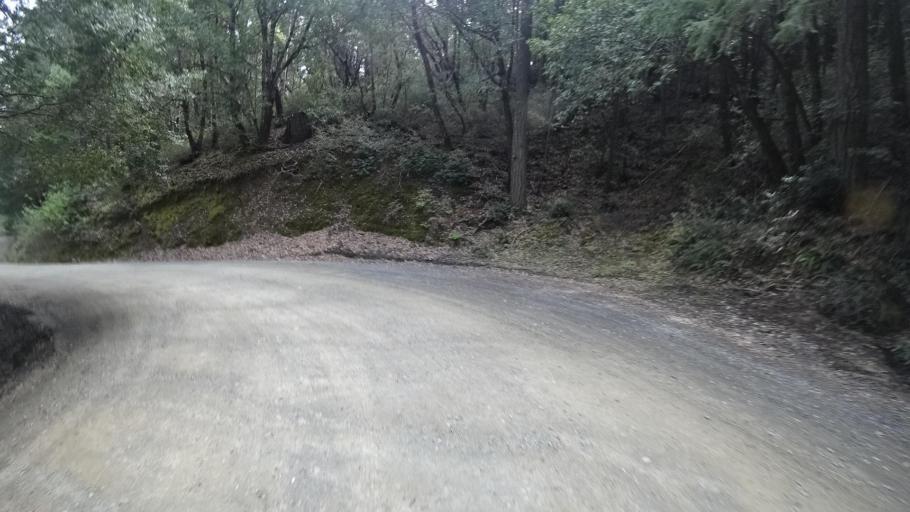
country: US
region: California
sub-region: Humboldt County
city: Redway
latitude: 40.0439
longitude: -123.8415
